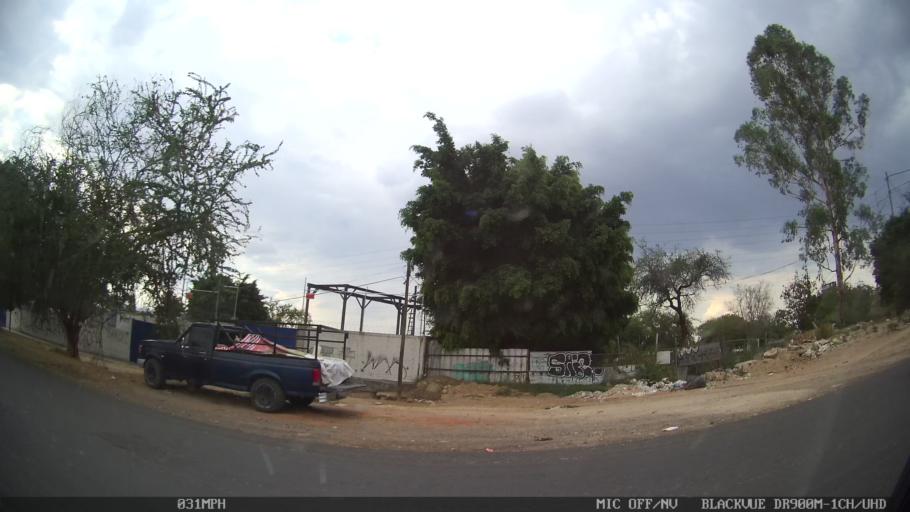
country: MX
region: Jalisco
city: Tlaquepaque
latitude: 20.6174
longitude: -103.2685
